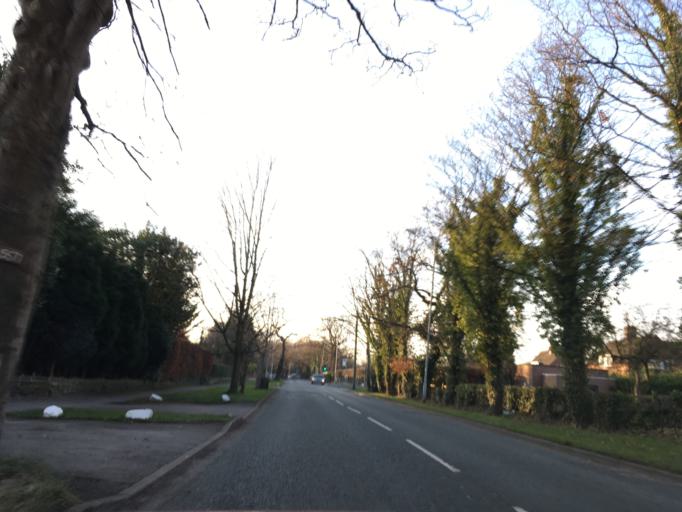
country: GB
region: England
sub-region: Borough of Stockport
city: Cheadle Hulme
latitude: 53.3591
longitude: -2.2123
